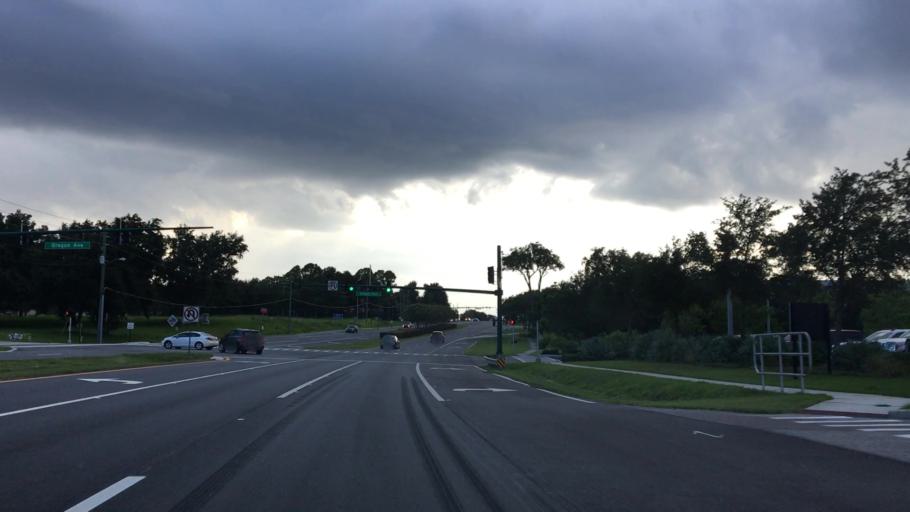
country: US
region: Florida
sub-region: Seminole County
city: Lake Mary
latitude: 28.7952
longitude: -81.3349
